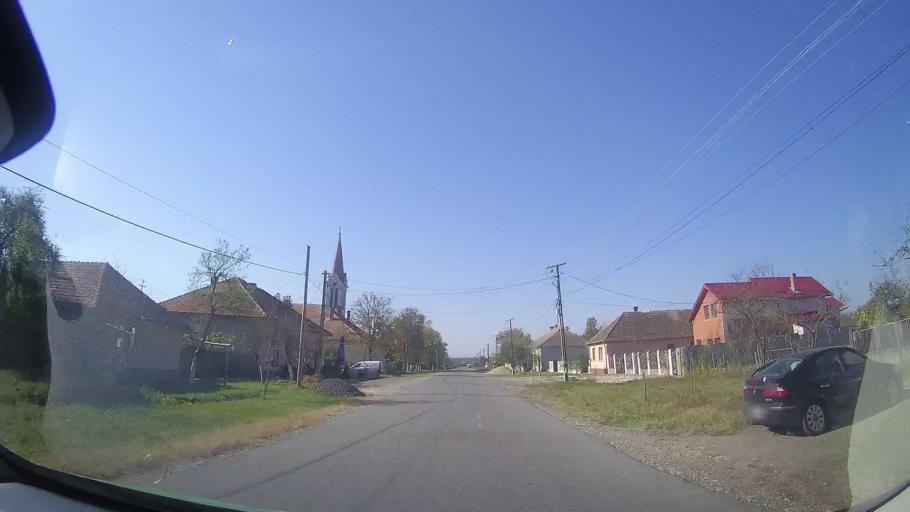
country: RO
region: Timis
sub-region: Comuna Ghizela
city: Ghizela
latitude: 45.8222
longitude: 21.7461
